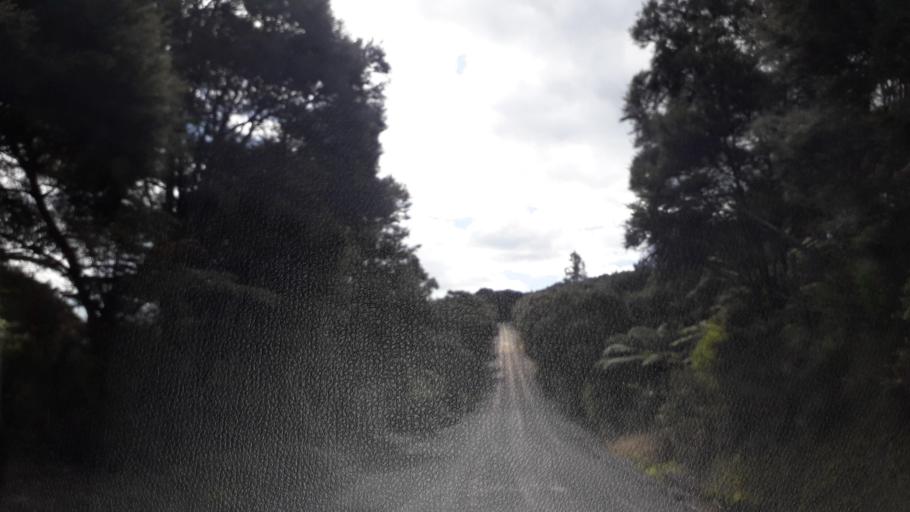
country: NZ
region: Northland
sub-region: Far North District
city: Paihia
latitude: -35.2996
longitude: 174.2192
